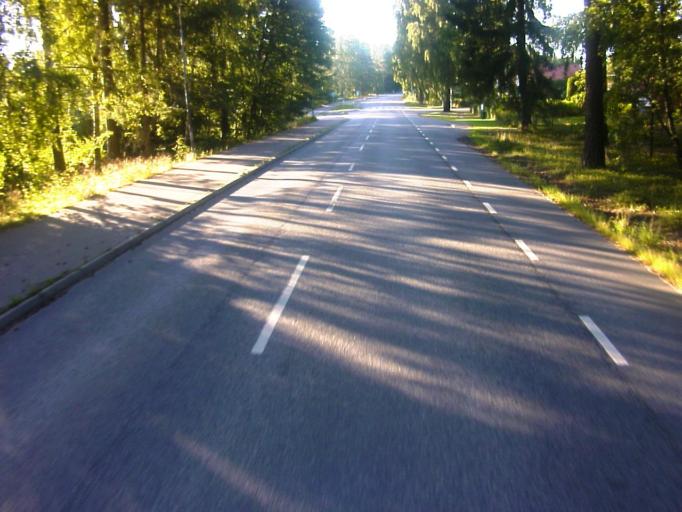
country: SE
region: Soedermanland
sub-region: Eskilstuna Kommun
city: Hallbybrunn
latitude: 59.3960
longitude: 16.4167
